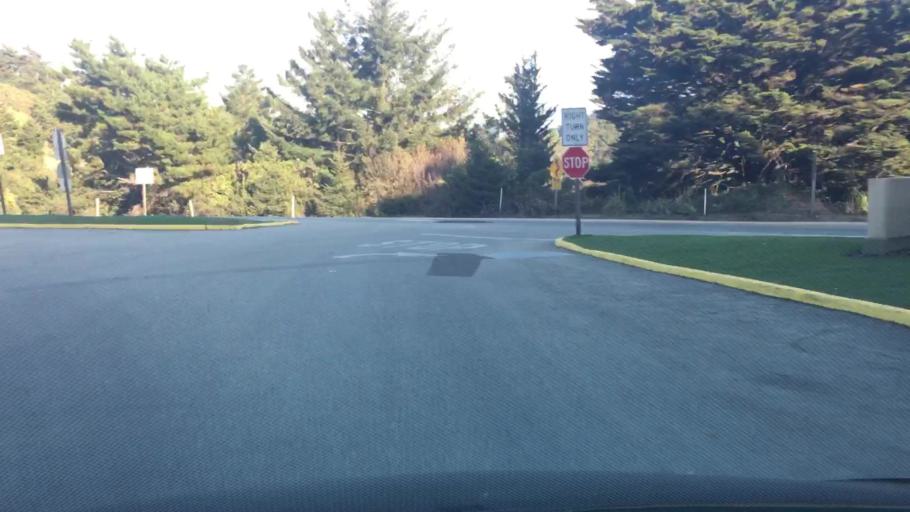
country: US
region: California
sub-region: San Mateo County
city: Highlands-Baywood Park
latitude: 37.4961
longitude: -122.3686
